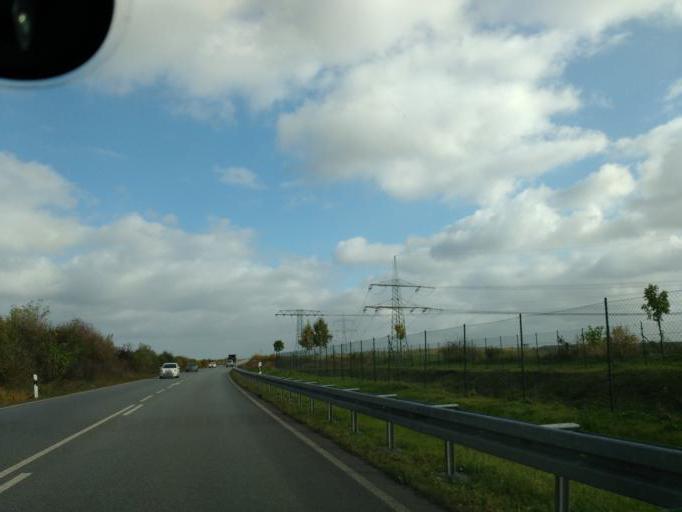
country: DE
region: Brandenburg
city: Altlandsberg
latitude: 52.5575
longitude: 13.7431
